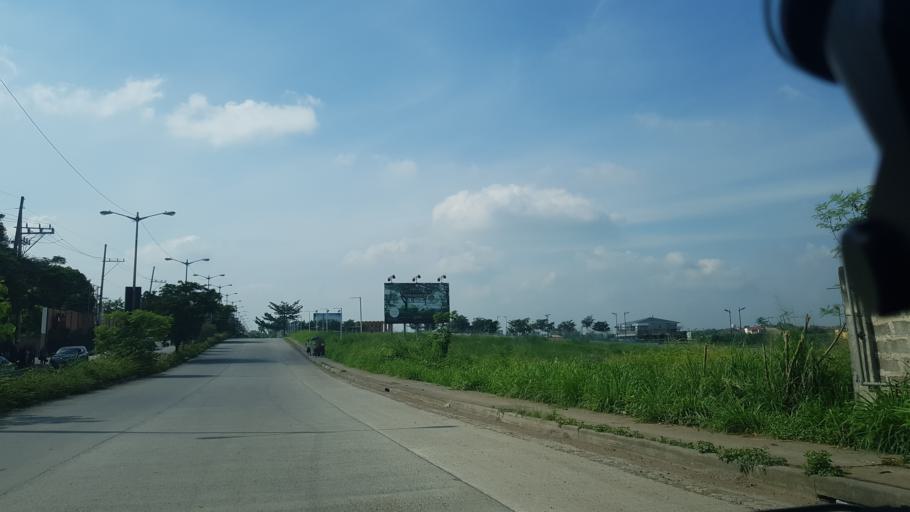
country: PH
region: Calabarzon
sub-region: Province of Laguna
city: San Pedro
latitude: 14.3901
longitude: 121.0095
